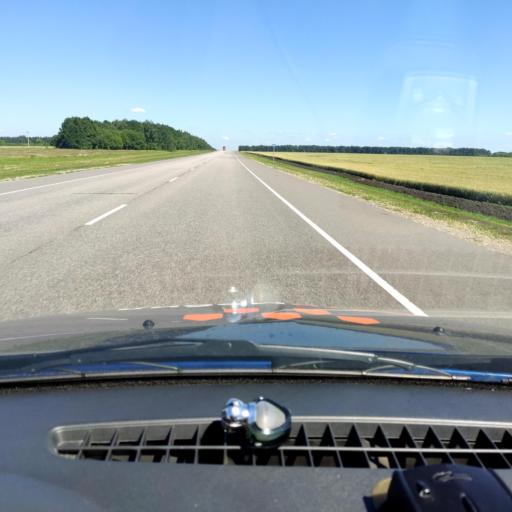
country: RU
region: Orjol
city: Pokrovskoye
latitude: 52.6234
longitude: 36.8014
